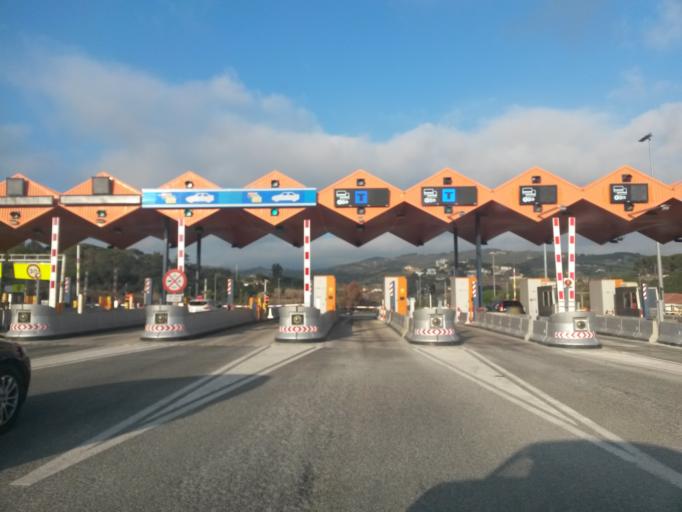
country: ES
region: Catalonia
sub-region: Provincia de Barcelona
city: Arenys de Mar
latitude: 41.5872
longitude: 2.5390
